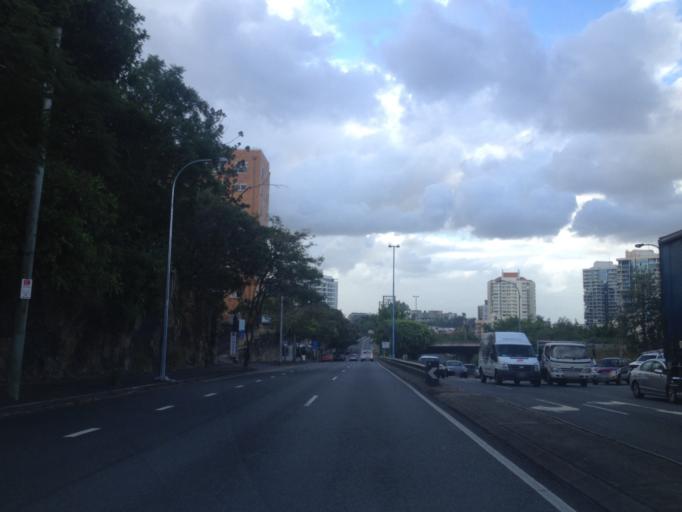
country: AU
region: Queensland
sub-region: Brisbane
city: Brisbane
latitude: -27.4752
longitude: 153.0356
